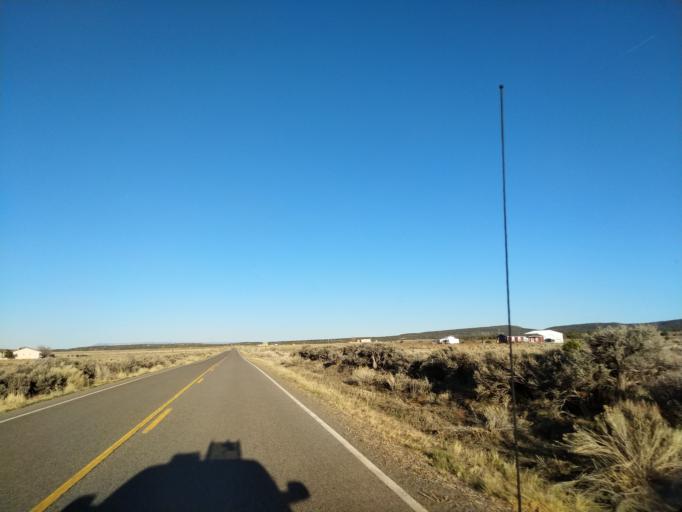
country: US
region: Colorado
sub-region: Mesa County
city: Redlands
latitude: 38.9902
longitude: -108.7618
